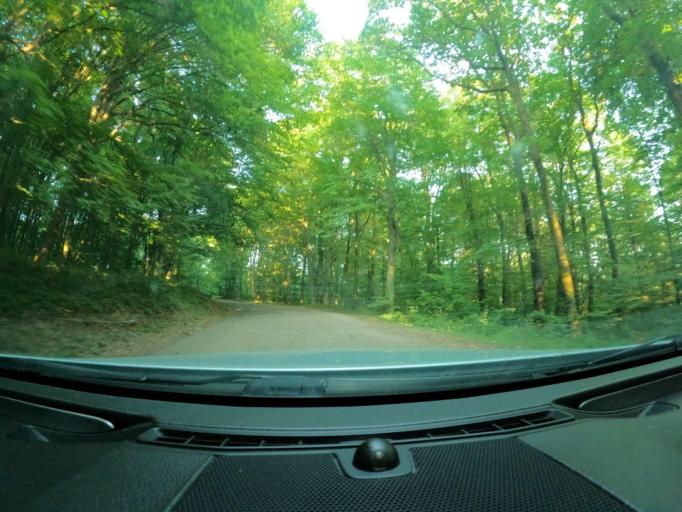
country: RS
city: Vrdnik
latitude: 45.1600
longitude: 19.7655
